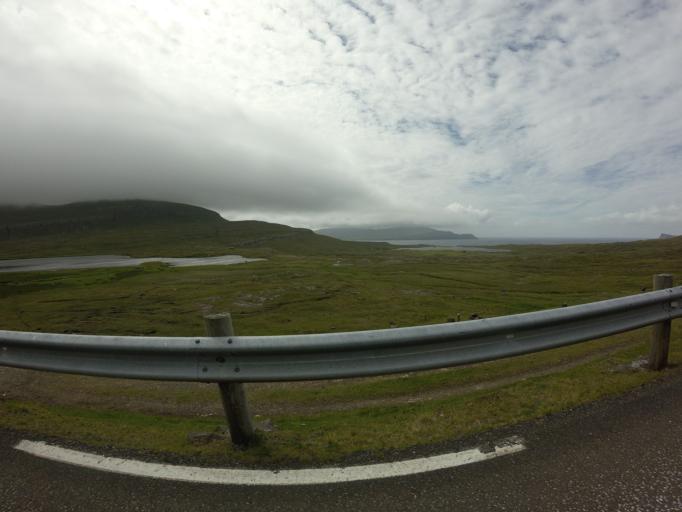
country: FO
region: Sandoy
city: Sandur
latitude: 61.8240
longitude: -6.7362
